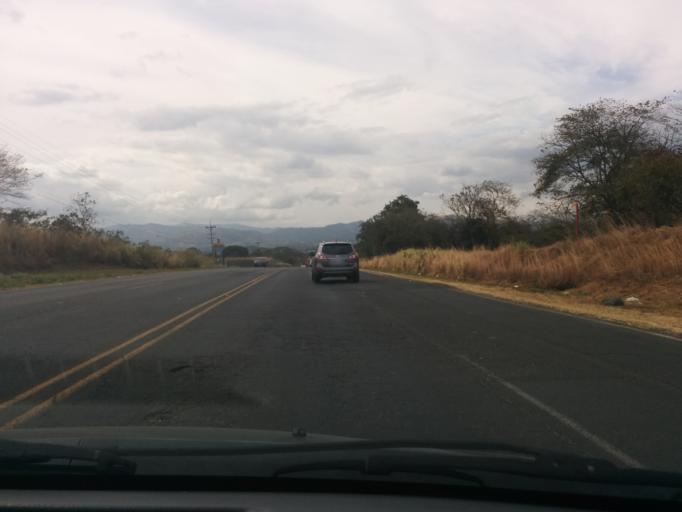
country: CR
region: Alajuela
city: Carrillos
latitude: 9.9982
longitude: -84.2757
